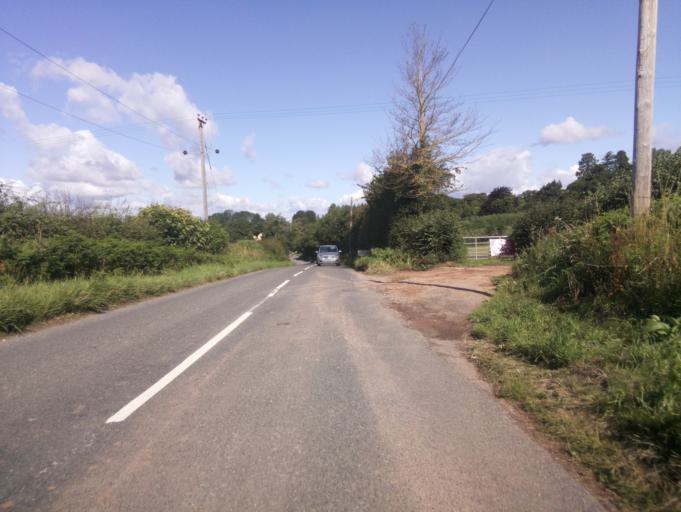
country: GB
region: England
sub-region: Herefordshire
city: Linton
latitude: 51.9388
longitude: -2.5185
